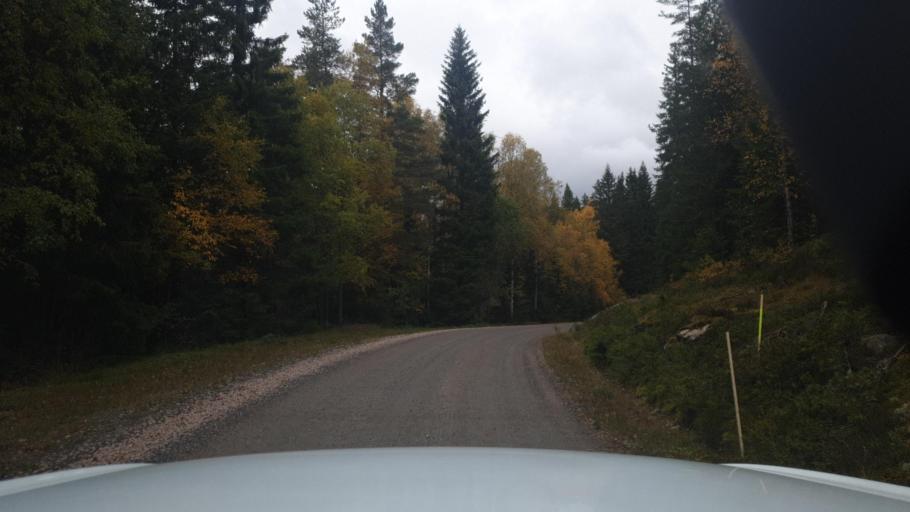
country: SE
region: Vaermland
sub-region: Eda Kommun
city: Charlottenberg
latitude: 60.1407
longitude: 12.5955
